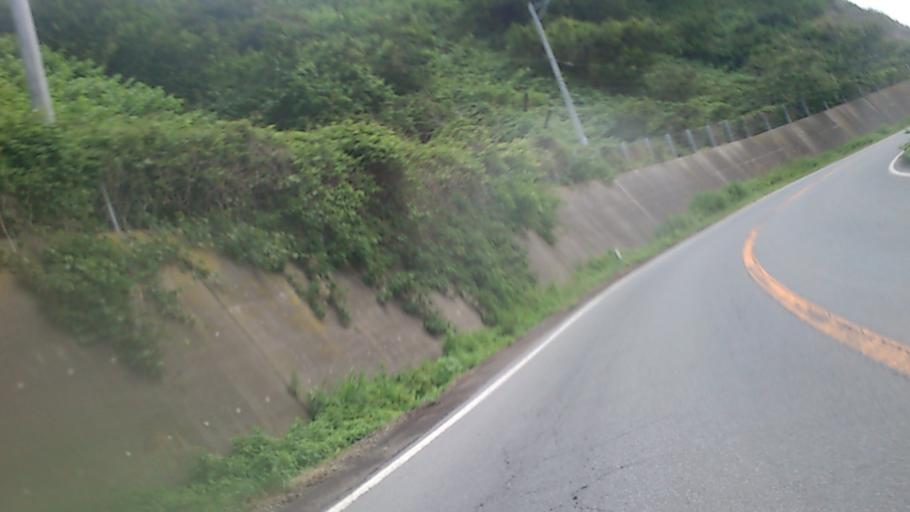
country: JP
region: Akita
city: Noshiromachi
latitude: 40.4383
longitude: 139.9416
